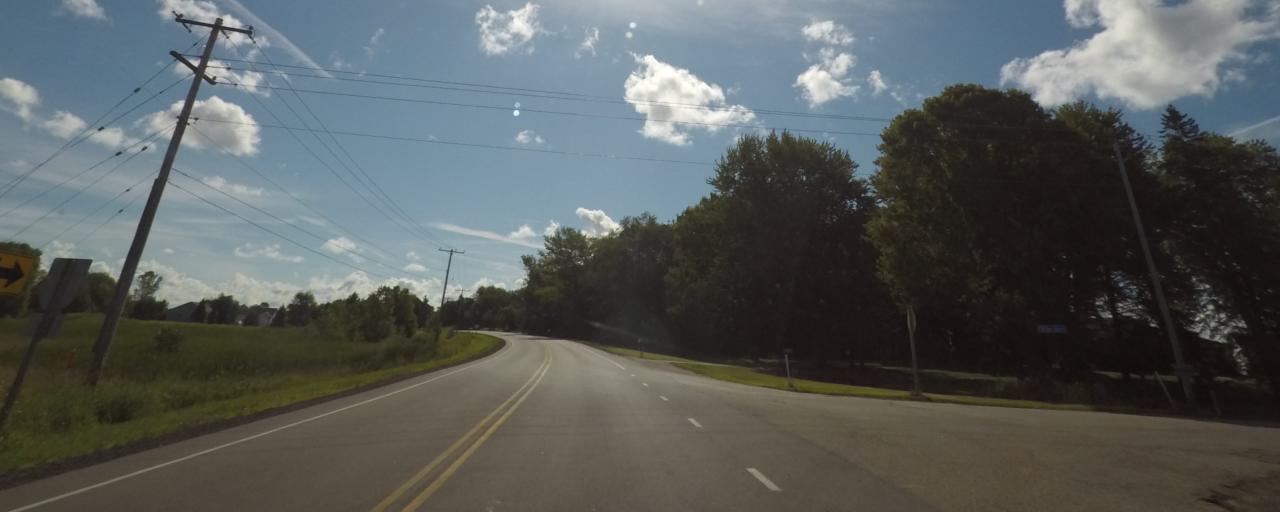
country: US
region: Wisconsin
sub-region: Waukesha County
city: Oconomowoc
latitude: 43.0749
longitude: -88.5553
